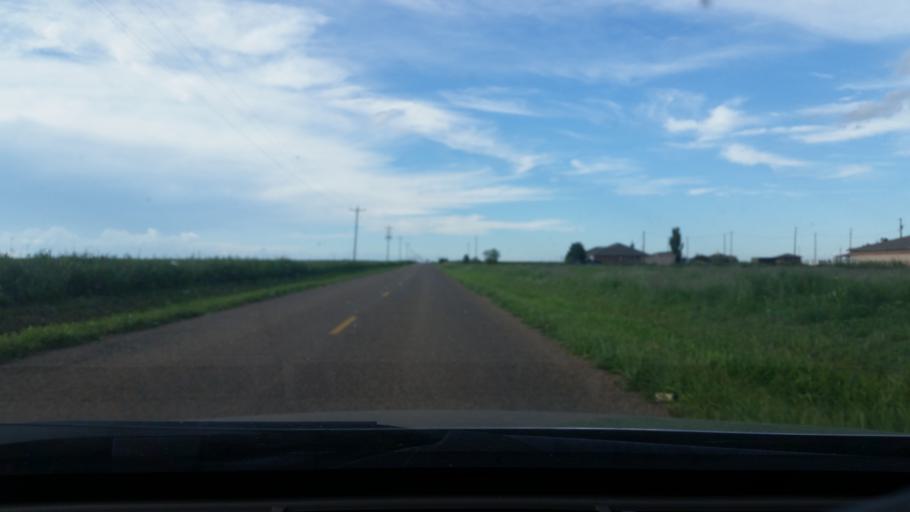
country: US
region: New Mexico
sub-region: Curry County
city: Clovis
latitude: 34.4595
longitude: -103.2140
